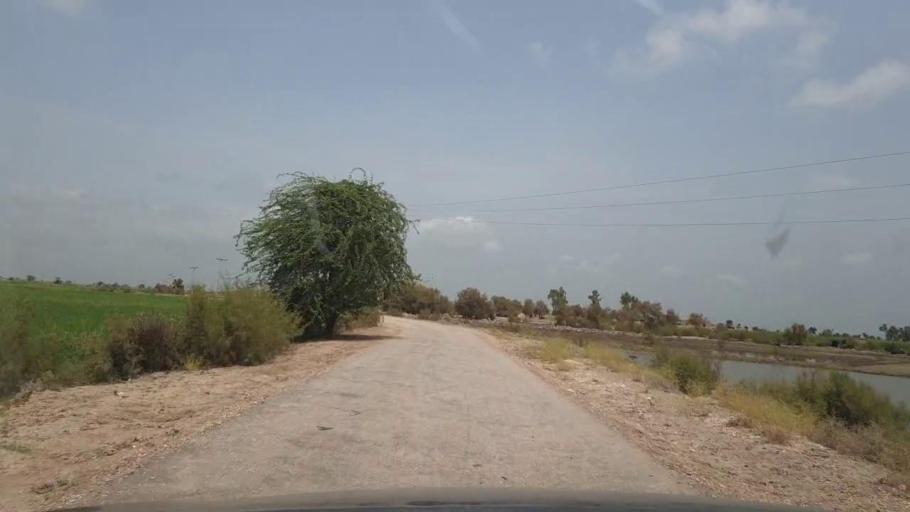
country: PK
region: Sindh
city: Ratodero
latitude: 27.9053
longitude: 68.3133
